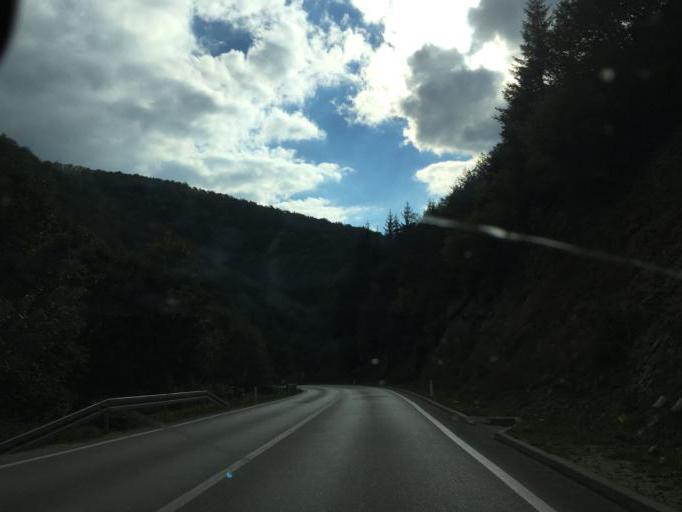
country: BA
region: Federation of Bosnia and Herzegovina
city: Novi Travnik
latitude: 44.0937
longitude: 17.5725
